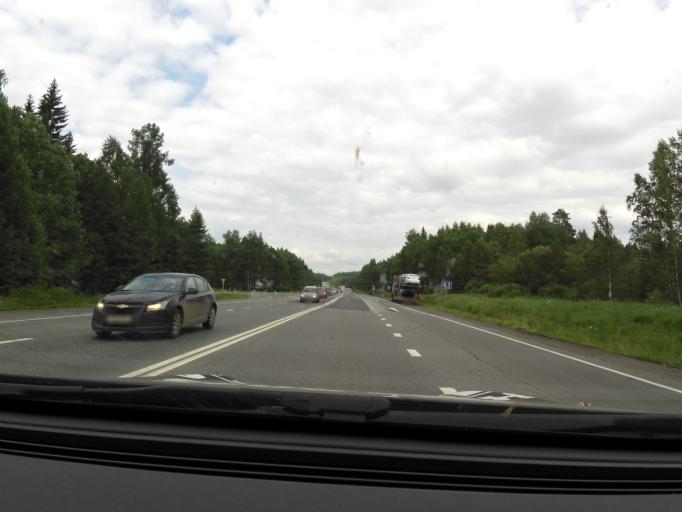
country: RU
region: Sverdlovsk
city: Druzhinino
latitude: 56.8454
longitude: 59.6800
